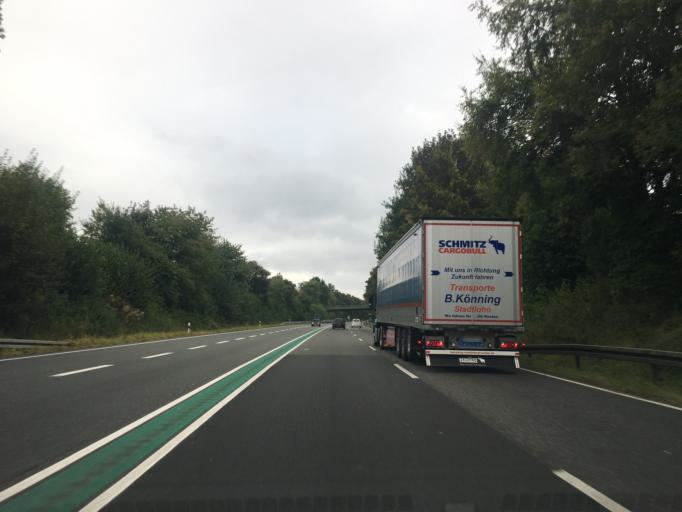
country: DE
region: North Rhine-Westphalia
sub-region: Regierungsbezirk Munster
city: Steinfurt
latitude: 52.1567
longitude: 7.3476
